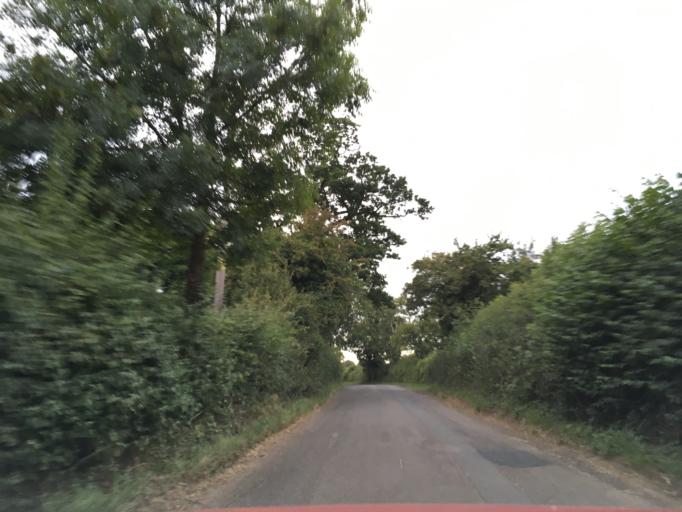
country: GB
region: England
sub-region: Wiltshire
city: Biddestone
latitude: 51.4514
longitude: -2.1987
